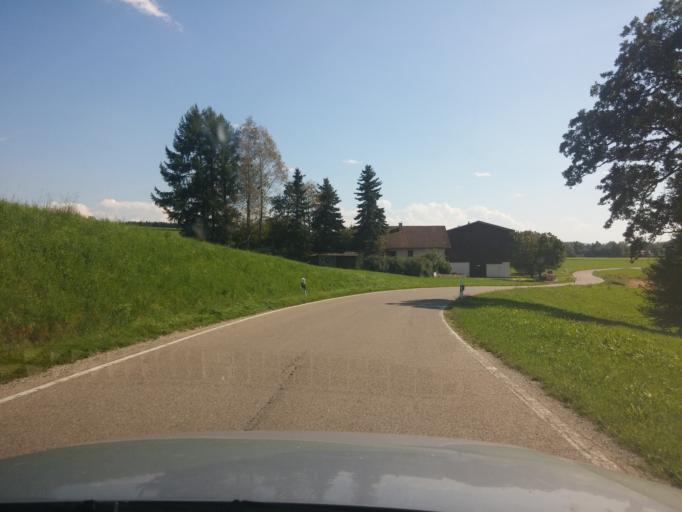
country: DE
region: Bavaria
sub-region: Swabia
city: Legau
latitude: 47.8322
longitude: 10.1026
